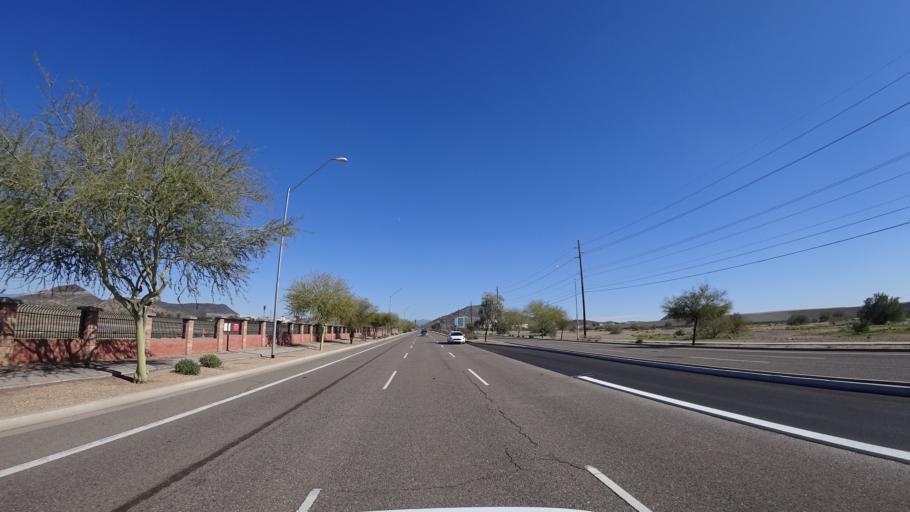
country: US
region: Arizona
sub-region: Maricopa County
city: Glendale
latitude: 33.6838
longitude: -112.0720
